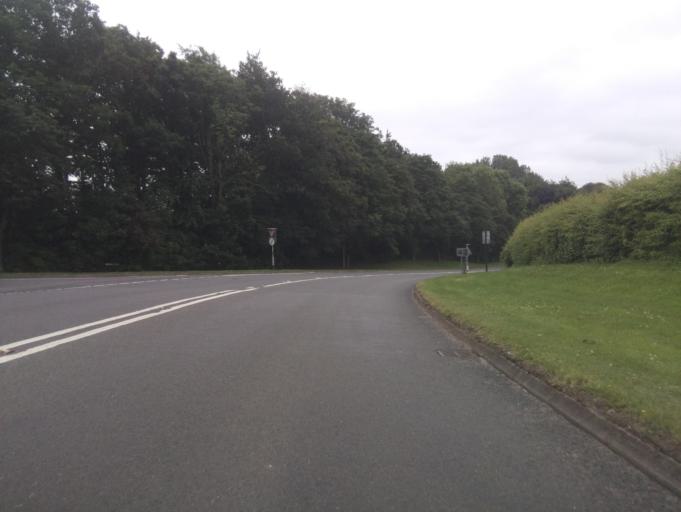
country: GB
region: England
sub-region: District of Rutland
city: Empingham
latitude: 52.6650
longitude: -0.5963
